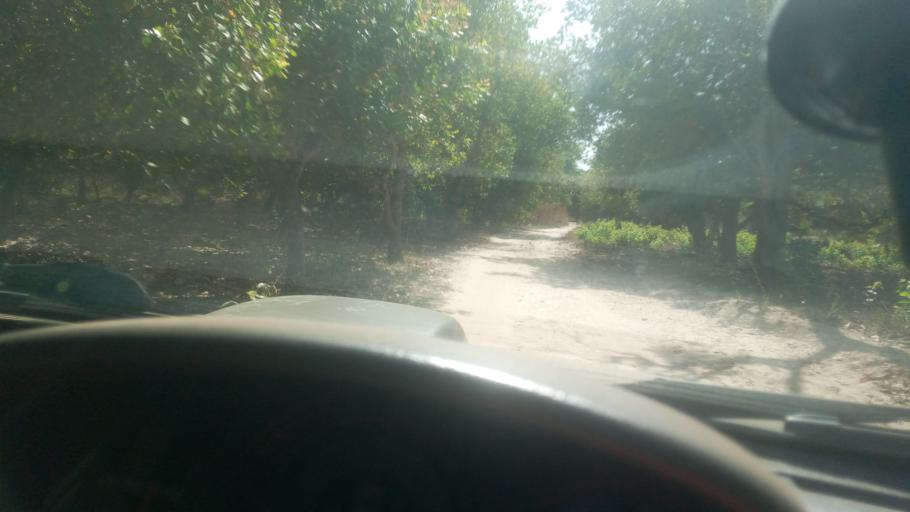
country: GW
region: Oio
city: Farim
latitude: 12.4470
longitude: -15.4323
